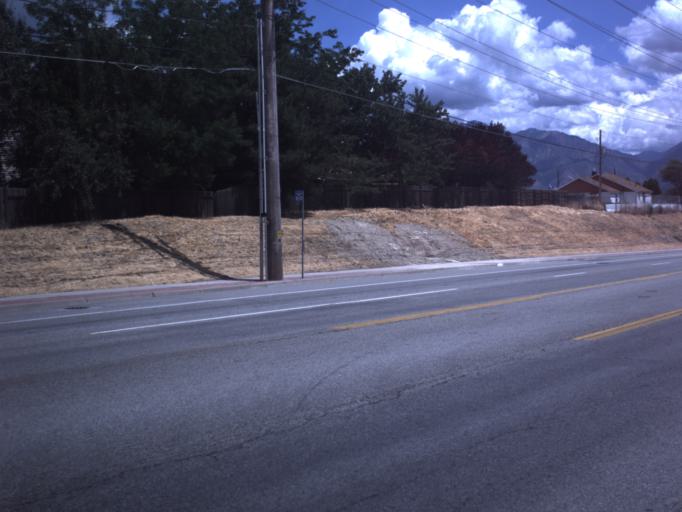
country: US
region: Utah
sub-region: Salt Lake County
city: South Jordan
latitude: 40.5877
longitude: -111.9221
